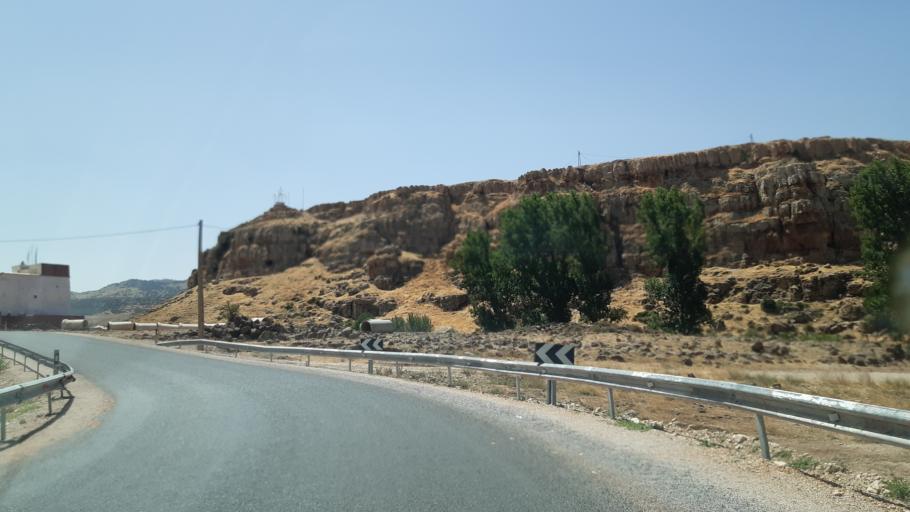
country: MA
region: Meknes-Tafilalet
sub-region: Ifrane
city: Azrou
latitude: 33.2392
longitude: -5.0661
